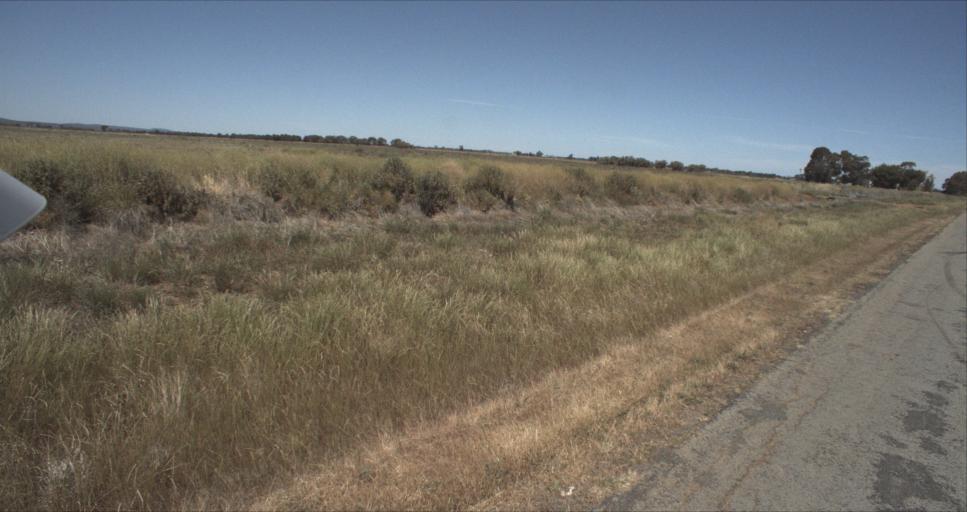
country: AU
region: New South Wales
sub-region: Leeton
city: Leeton
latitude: -34.5083
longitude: 146.3446
